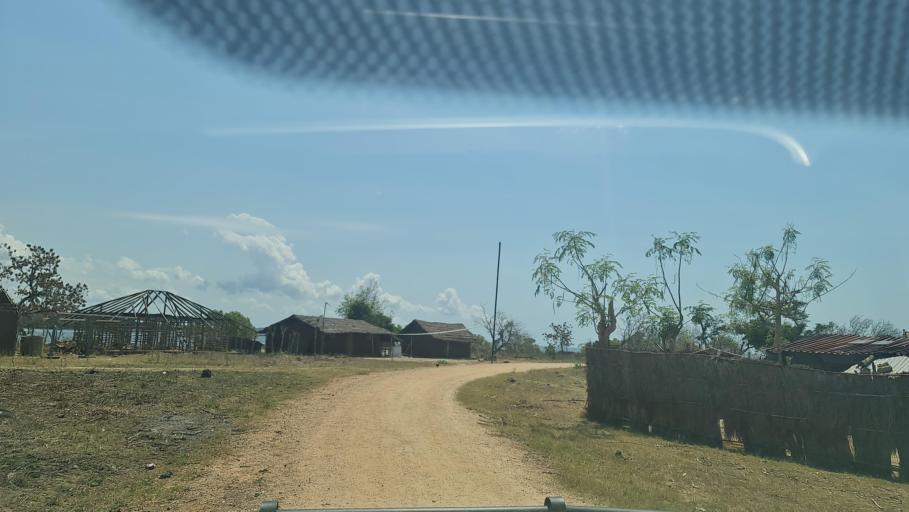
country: MZ
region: Nampula
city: Ilha de Mocambique
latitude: -15.1792
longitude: 40.5122
